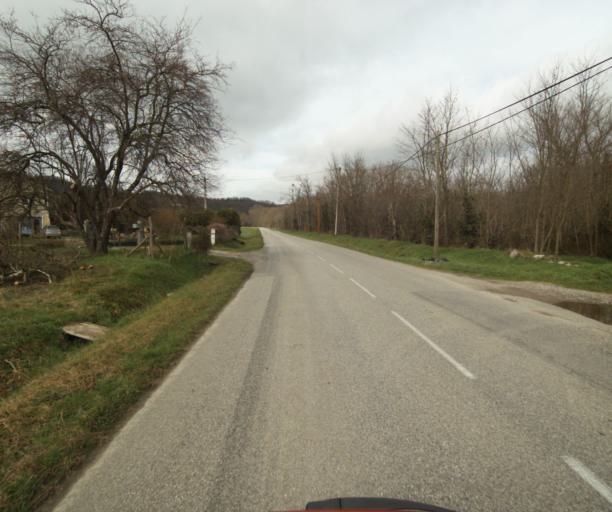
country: FR
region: Midi-Pyrenees
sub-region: Departement de l'Ariege
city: Pamiers
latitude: 43.1293
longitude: 1.6039
